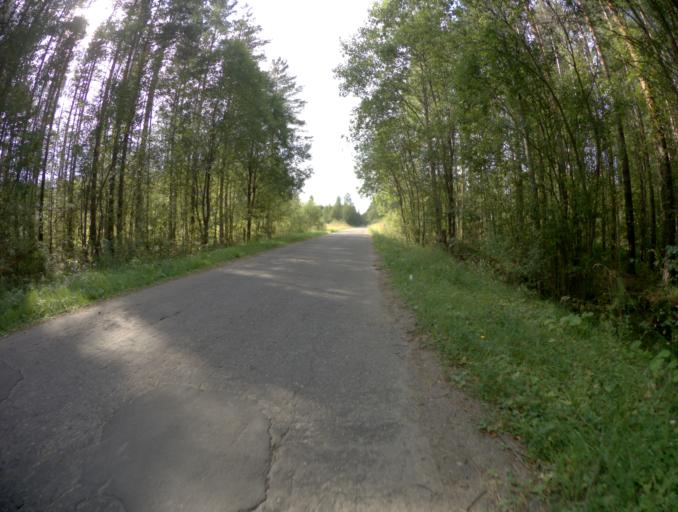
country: RU
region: Vladimir
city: Golovino
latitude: 55.9660
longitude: 40.4152
